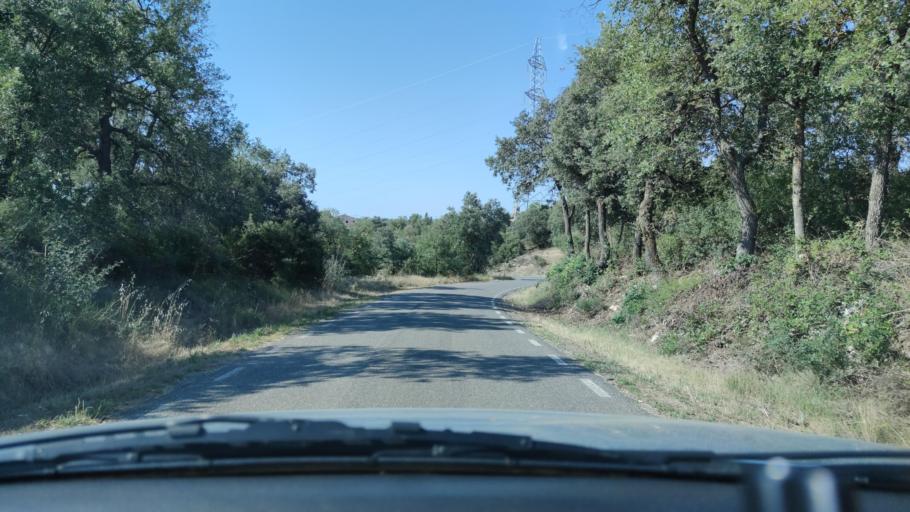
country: ES
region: Catalonia
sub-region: Provincia de Barcelona
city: Pujalt
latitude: 41.7157
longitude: 1.3678
